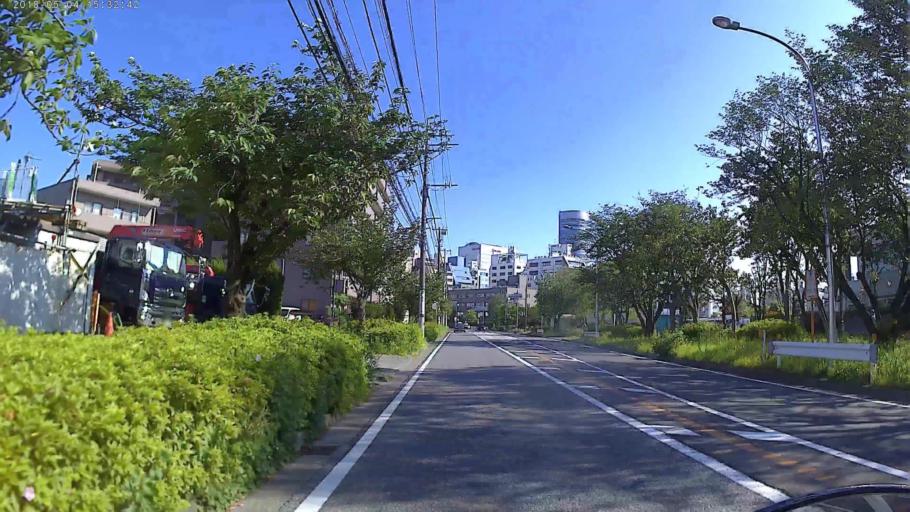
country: JP
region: Kanagawa
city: Yokohama
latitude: 35.5165
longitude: 139.6207
